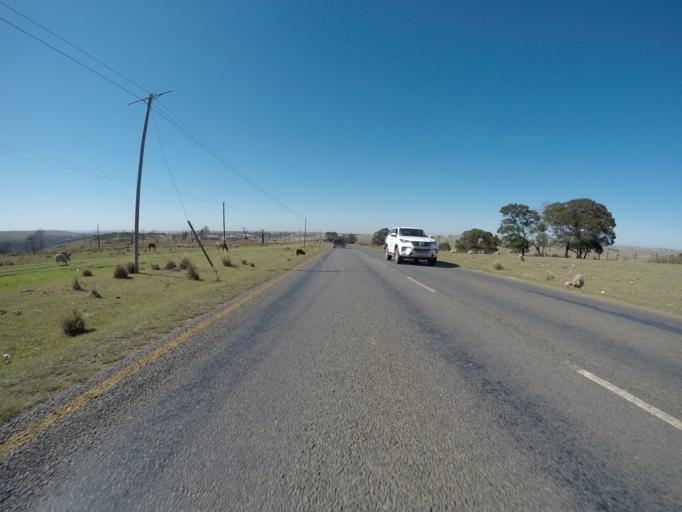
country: ZA
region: Eastern Cape
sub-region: OR Tambo District Municipality
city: Mthatha
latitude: -31.7979
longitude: 28.7454
